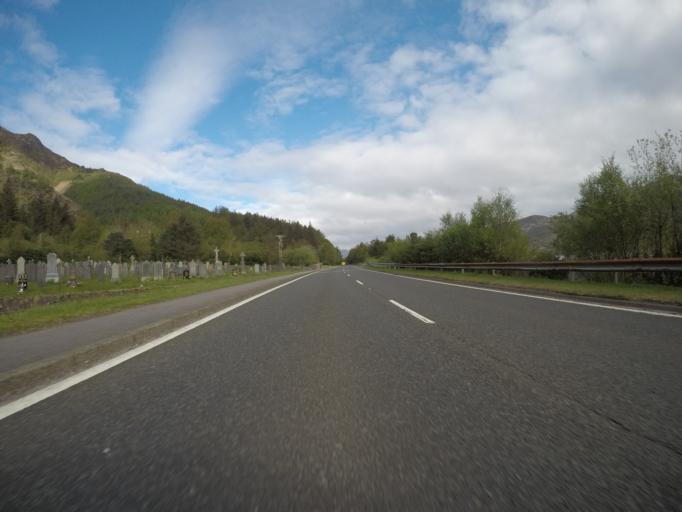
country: GB
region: Scotland
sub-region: Highland
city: Fort William
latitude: 56.6782
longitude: -5.1552
